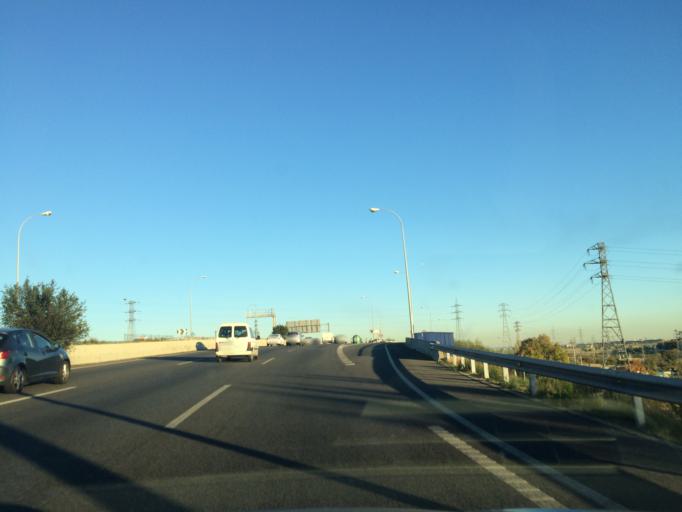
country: ES
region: Madrid
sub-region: Provincia de Madrid
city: Alcorcon
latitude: 40.3616
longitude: -3.8107
